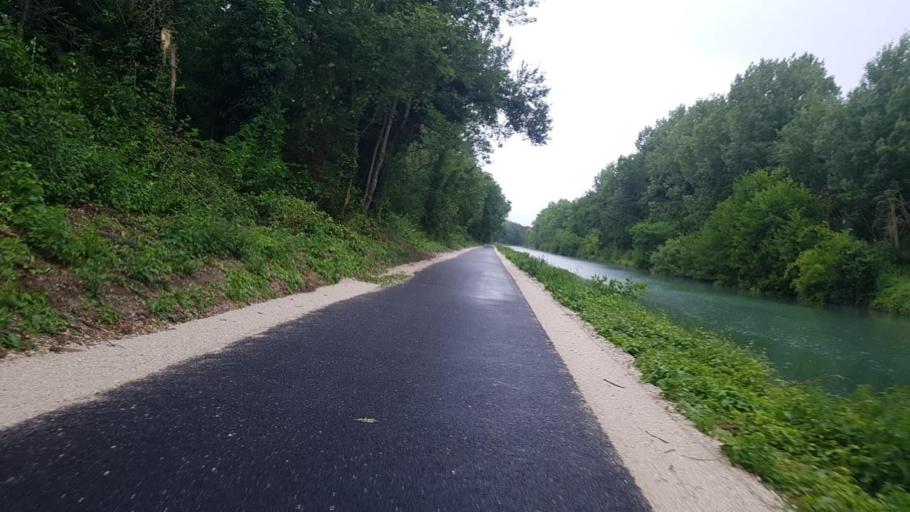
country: FR
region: Champagne-Ardenne
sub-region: Departement de la Marne
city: Sarry
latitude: 48.8672
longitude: 4.4637
